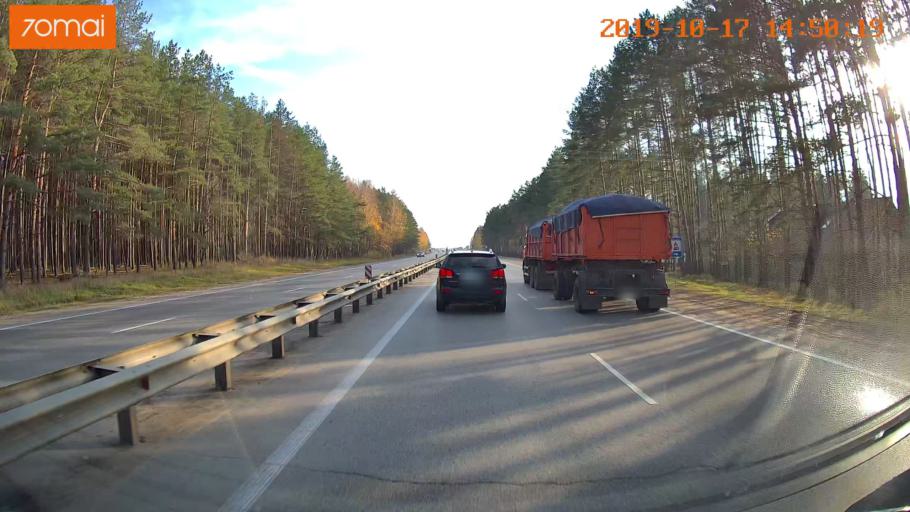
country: RU
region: Rjazan
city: Polyany
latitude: 54.7355
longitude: 39.8417
